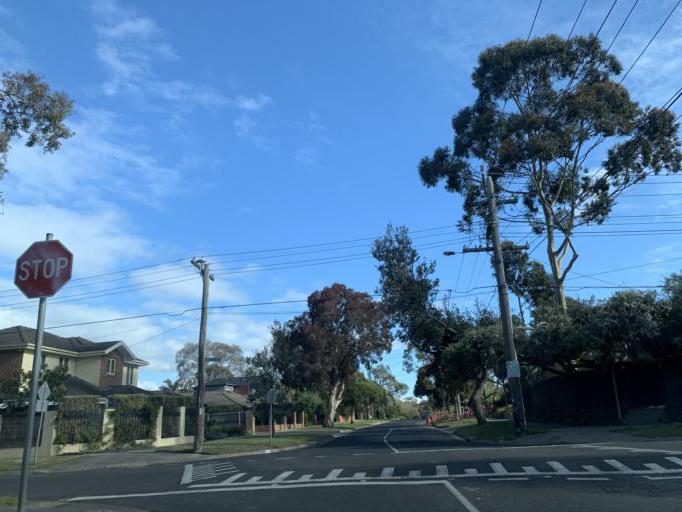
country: AU
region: Victoria
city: Beaumaris
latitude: -37.9809
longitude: 145.0433
